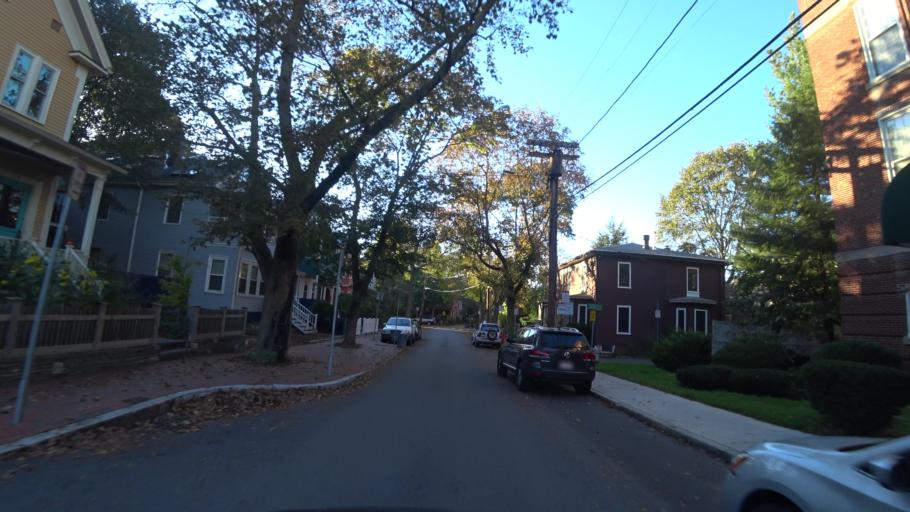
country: US
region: Massachusetts
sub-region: Middlesex County
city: Cambridge
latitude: 42.3899
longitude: -71.1249
